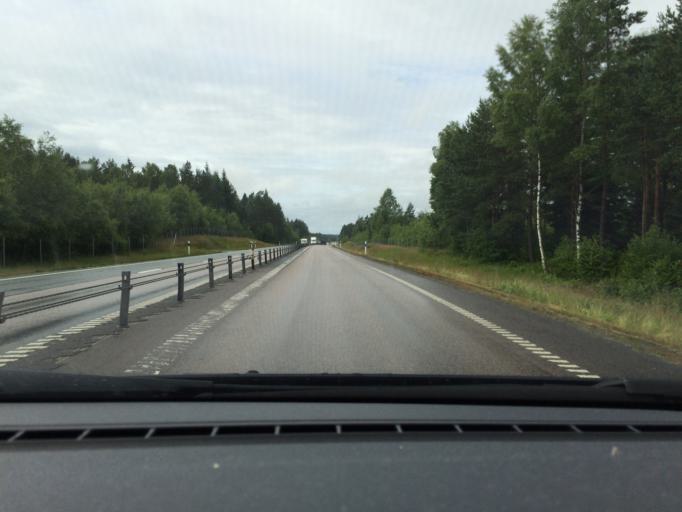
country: SE
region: Joenkoeping
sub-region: Varnamo Kommun
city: Forsheda
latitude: 57.1722
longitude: 13.9042
